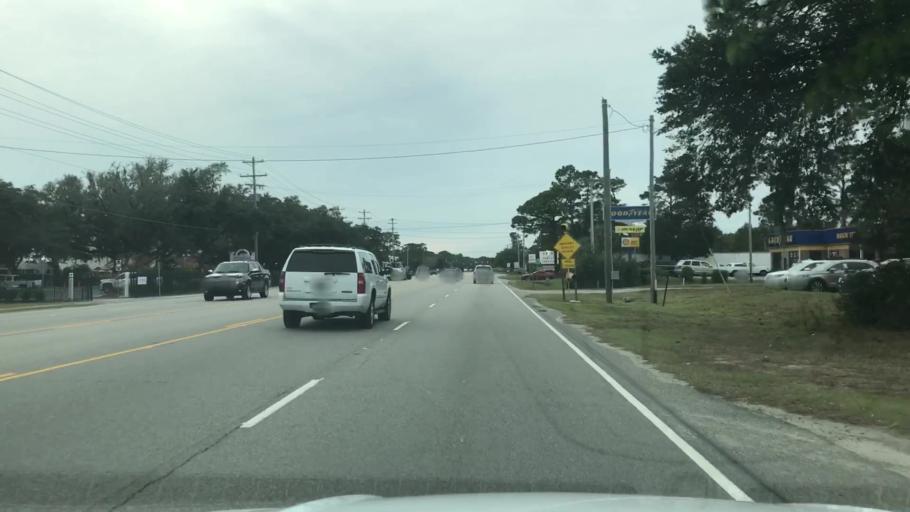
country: US
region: South Carolina
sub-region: Georgetown County
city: Murrells Inlet
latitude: 33.4326
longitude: -79.1403
